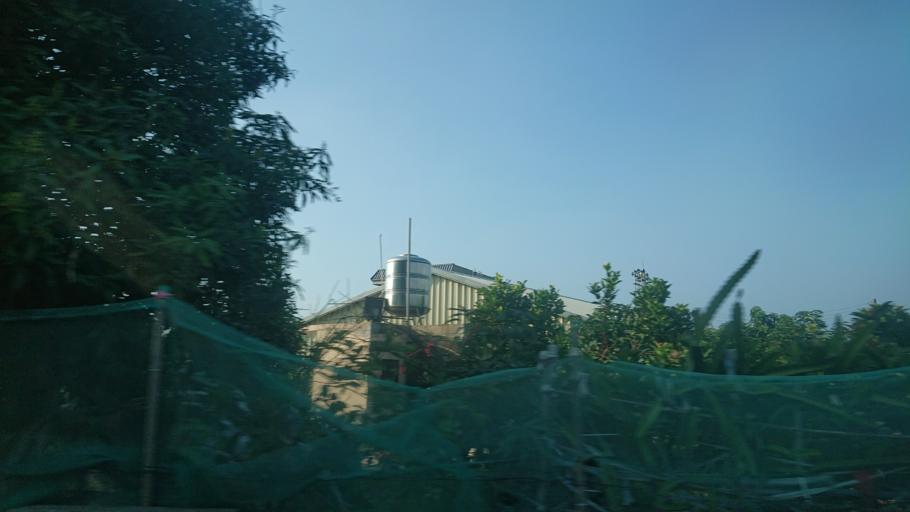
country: TW
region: Taiwan
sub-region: Tainan
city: Tainan
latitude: 23.1266
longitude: 120.2273
